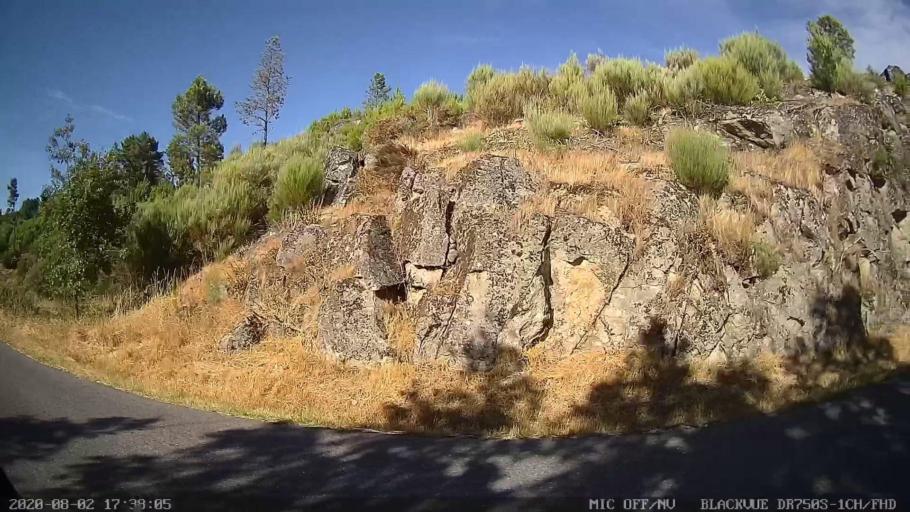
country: PT
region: Vila Real
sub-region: Murca
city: Murca
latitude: 41.3702
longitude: -7.5416
